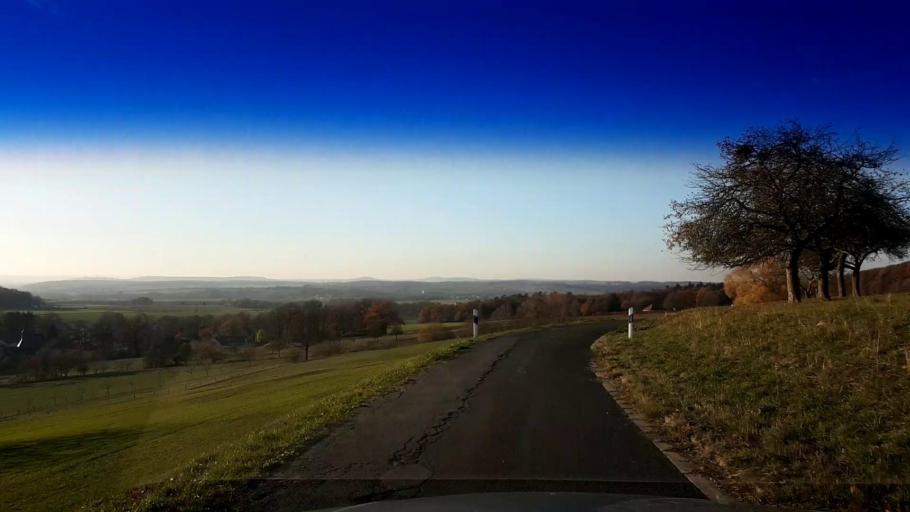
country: DE
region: Bavaria
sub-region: Upper Franconia
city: Schesslitz
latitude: 49.9509
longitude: 11.0432
